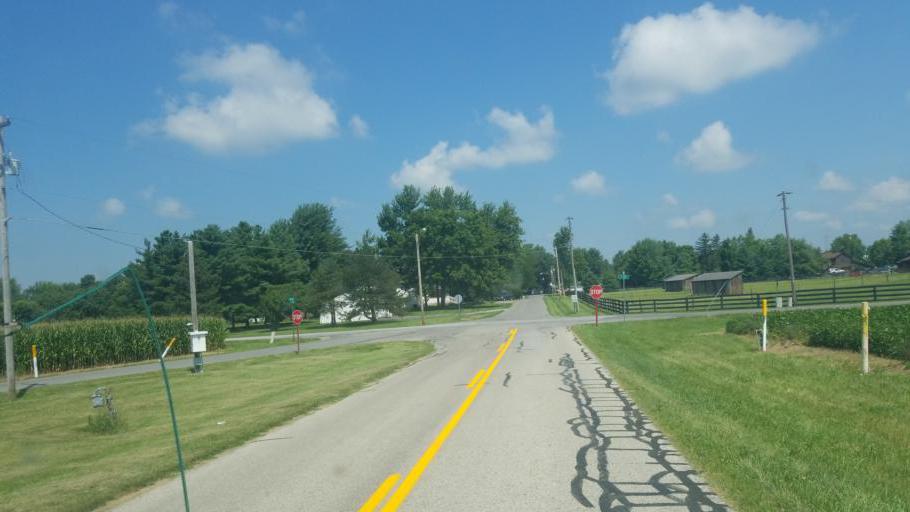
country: US
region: Ohio
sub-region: Hardin County
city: Ada
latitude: 40.7024
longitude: -83.9181
